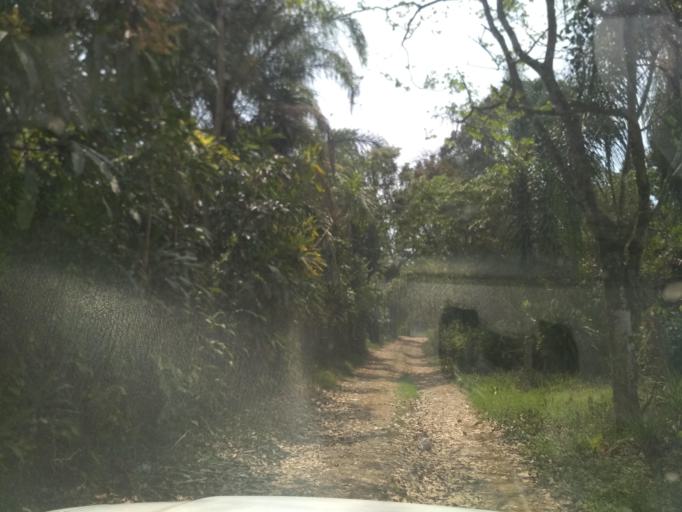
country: MX
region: Veracruz
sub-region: Cordoba
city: San Jose de Tapia
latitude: 18.8538
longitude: -96.9787
